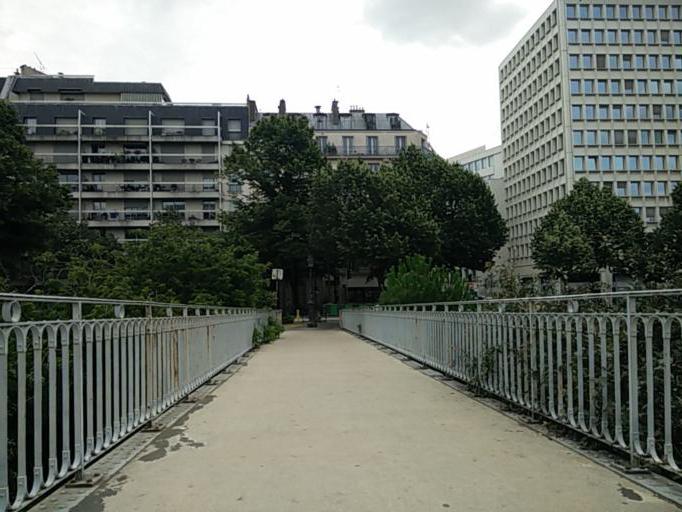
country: FR
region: Ile-de-France
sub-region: Paris
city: Paris
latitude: 48.8492
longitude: 2.3674
